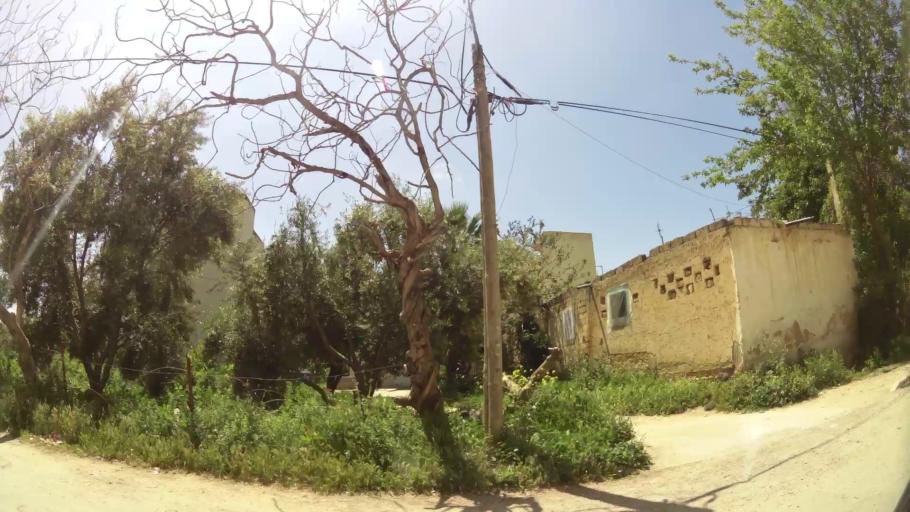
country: MA
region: Fes-Boulemane
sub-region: Fes
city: Fes
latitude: 34.0263
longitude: -5.0470
